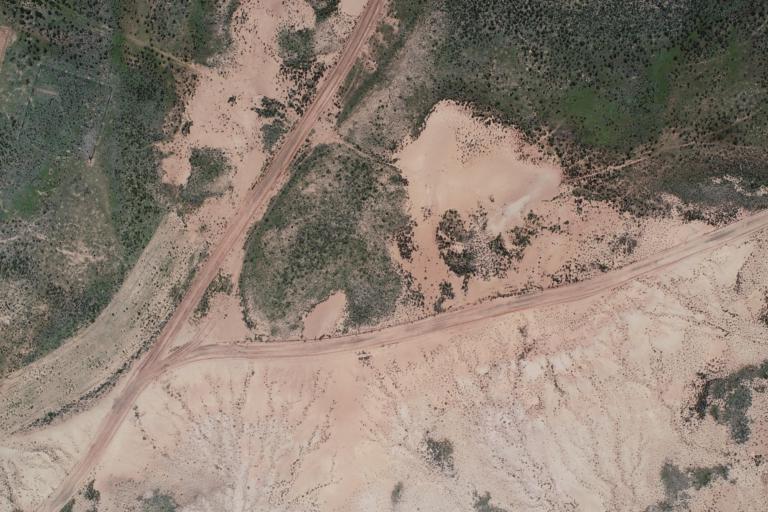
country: BO
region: La Paz
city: Curahuara de Carangas
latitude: -17.2953
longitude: -68.4953
